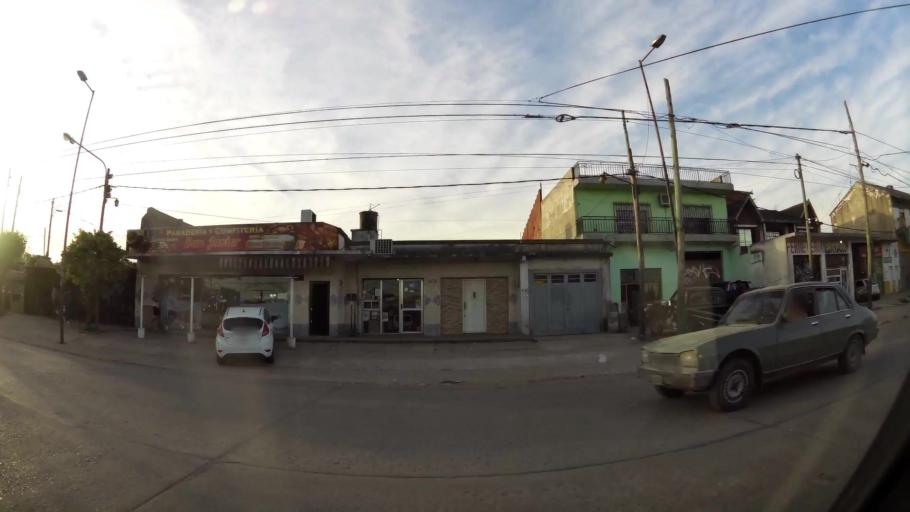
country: AR
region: Buenos Aires
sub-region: Partido de Almirante Brown
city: Adrogue
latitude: -34.7859
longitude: -58.3466
